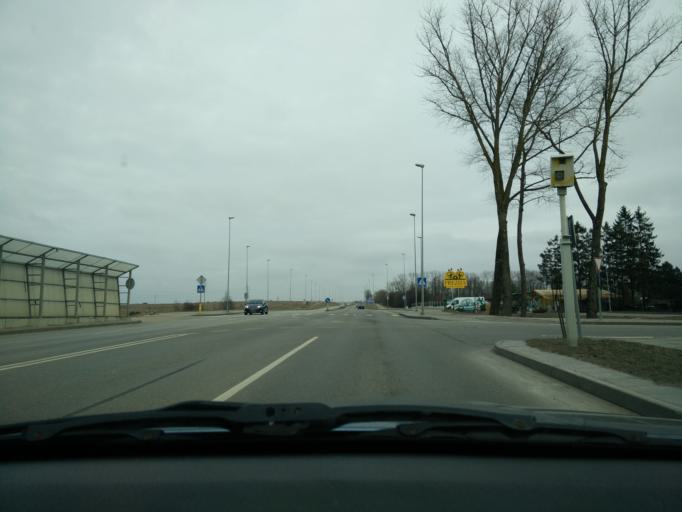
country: LT
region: Klaipedos apskritis
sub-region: Klaipeda
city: Klaipeda
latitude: 55.7272
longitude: 21.1718
